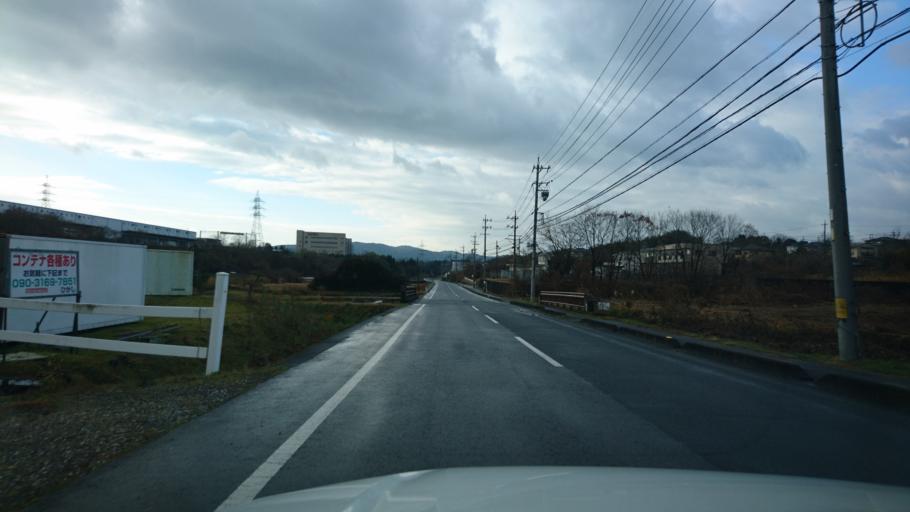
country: JP
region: Mie
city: Ueno-ebisumachi
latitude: 34.7245
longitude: 136.0815
